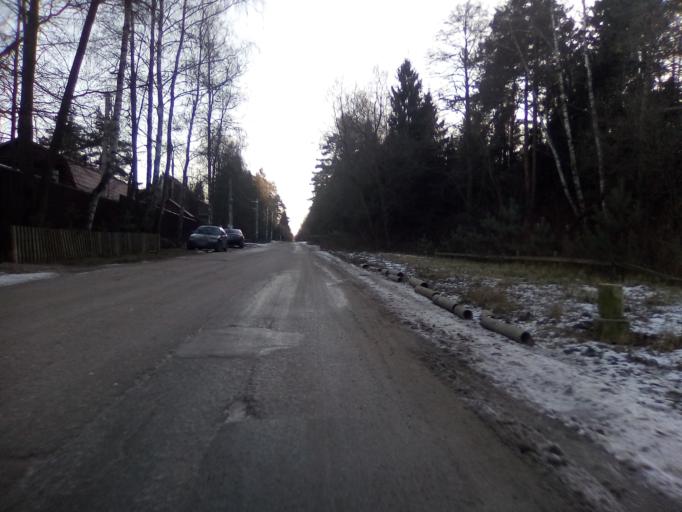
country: RU
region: Moskovskaya
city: Zhavoronki
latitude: 55.6409
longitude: 37.1449
